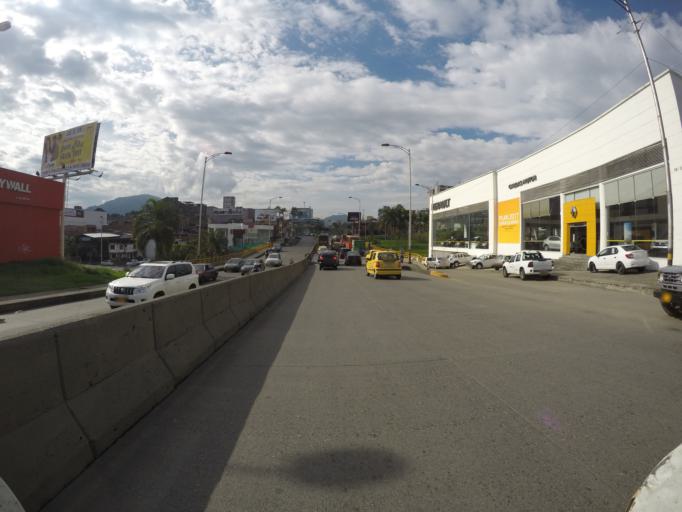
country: CO
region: Risaralda
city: Pereira
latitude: 4.8062
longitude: -75.6934
